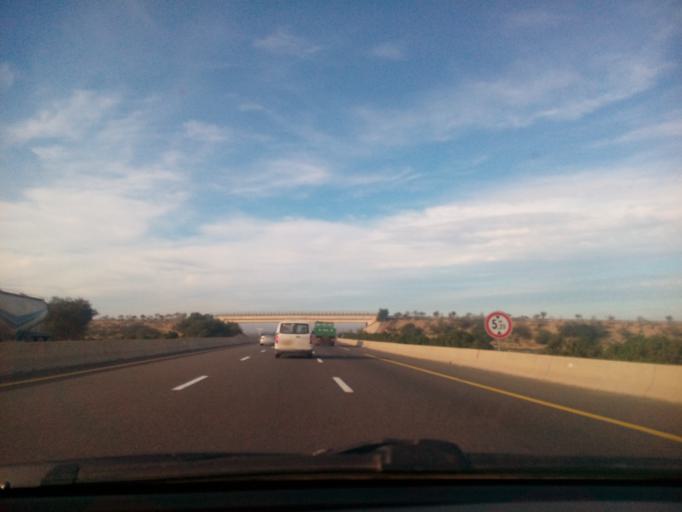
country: DZ
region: Mascara
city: Sig
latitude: 35.5913
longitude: -0.0552
